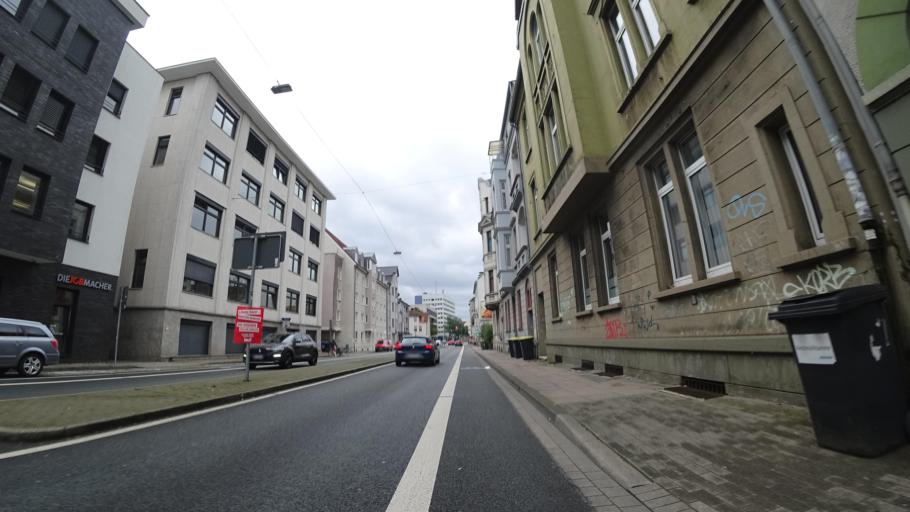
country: DE
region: North Rhine-Westphalia
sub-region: Regierungsbezirk Detmold
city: Bielefeld
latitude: 52.0262
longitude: 8.5397
